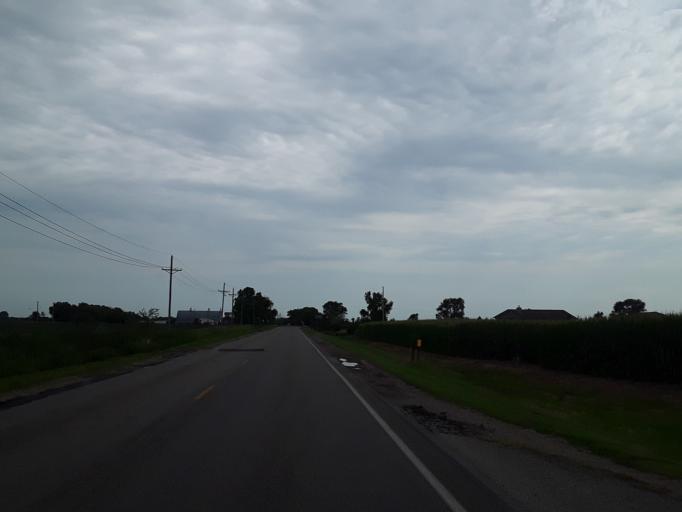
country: US
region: Nebraska
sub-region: Saunders County
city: Yutan
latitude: 41.2223
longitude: -96.3303
